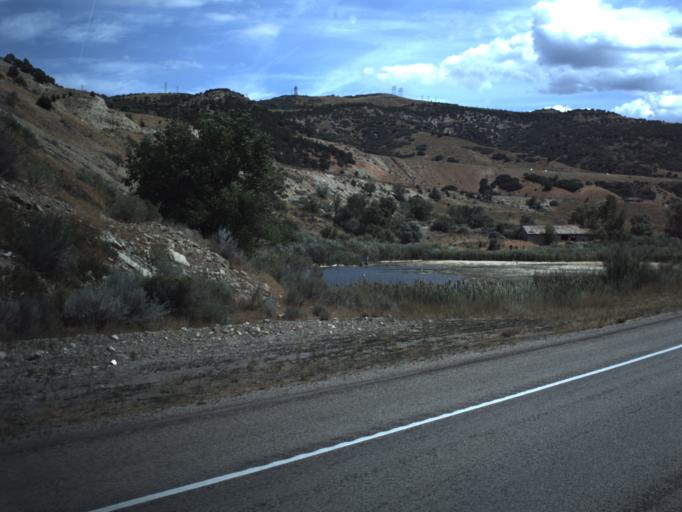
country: US
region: Utah
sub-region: Utah County
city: Woodland Hills
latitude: 39.9941
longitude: -111.4927
